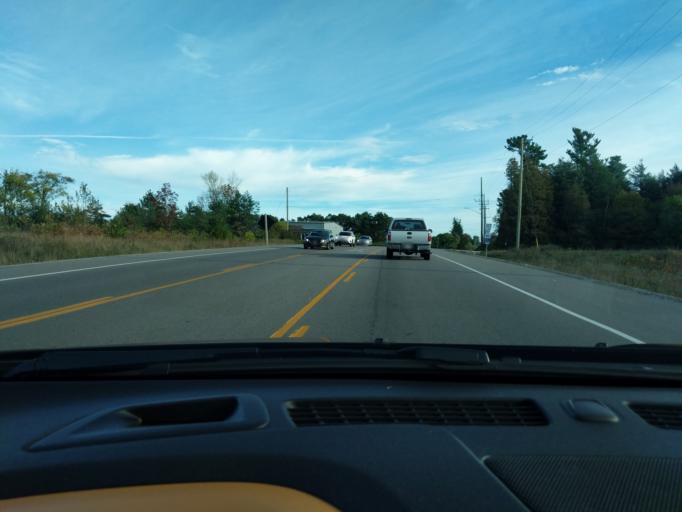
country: CA
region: Ontario
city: Barrie
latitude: 44.4261
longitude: -79.7639
